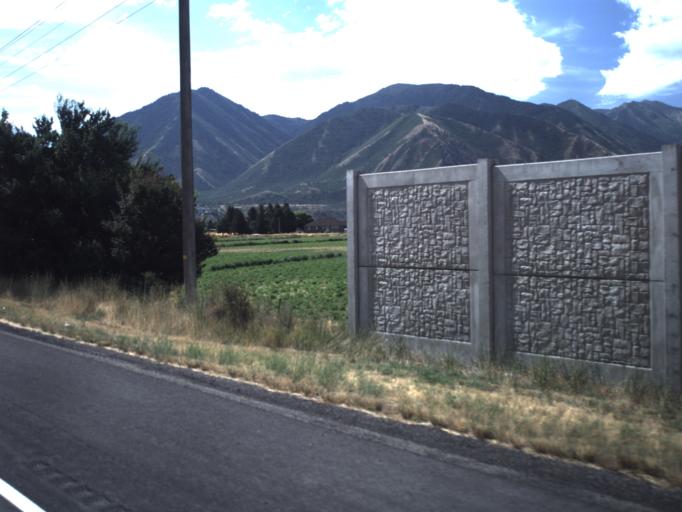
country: US
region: Utah
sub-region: Utah County
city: Spanish Fork
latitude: 40.1041
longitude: -111.6214
